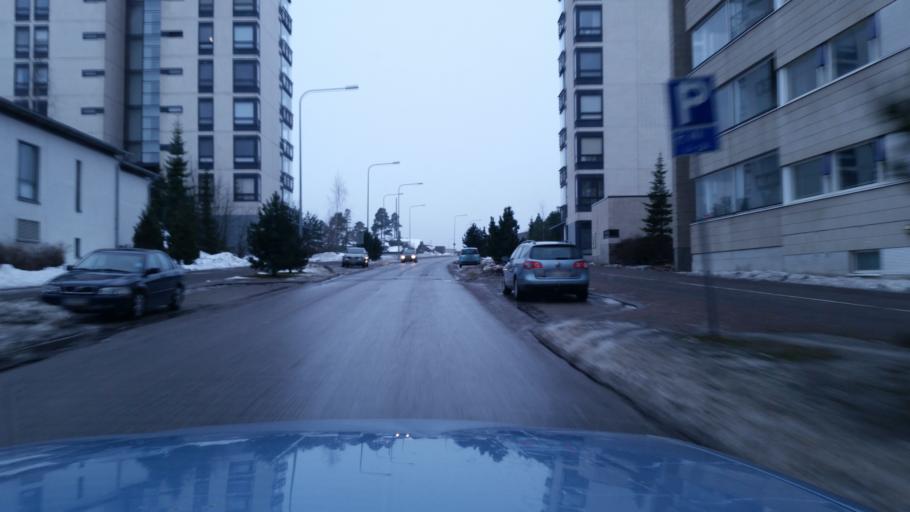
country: FI
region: Uusimaa
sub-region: Helsinki
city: Vantaa
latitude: 60.2299
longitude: 24.9967
